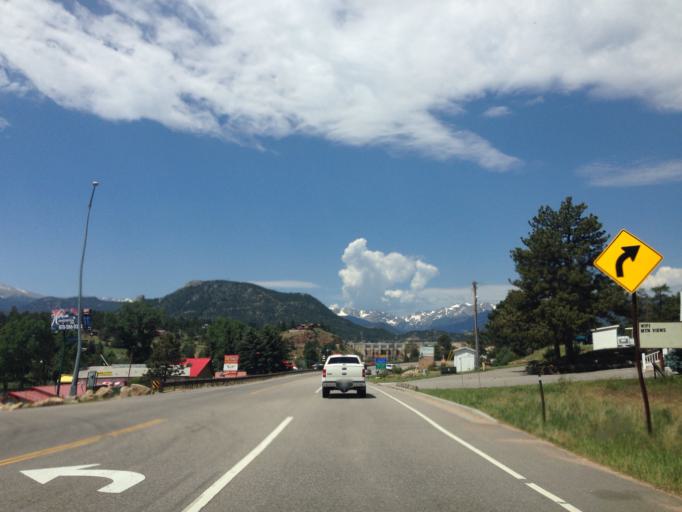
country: US
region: Colorado
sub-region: Larimer County
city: Estes Park
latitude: 40.3768
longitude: -105.4805
